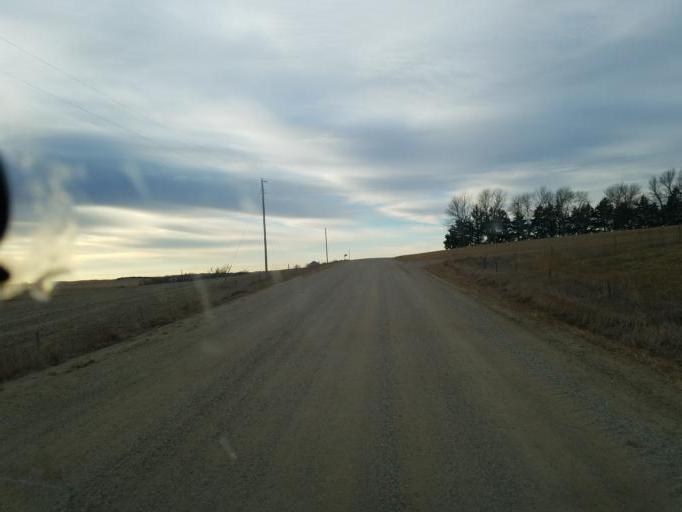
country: US
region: Nebraska
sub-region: Knox County
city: Bloomfield
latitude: 42.5788
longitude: -97.6815
